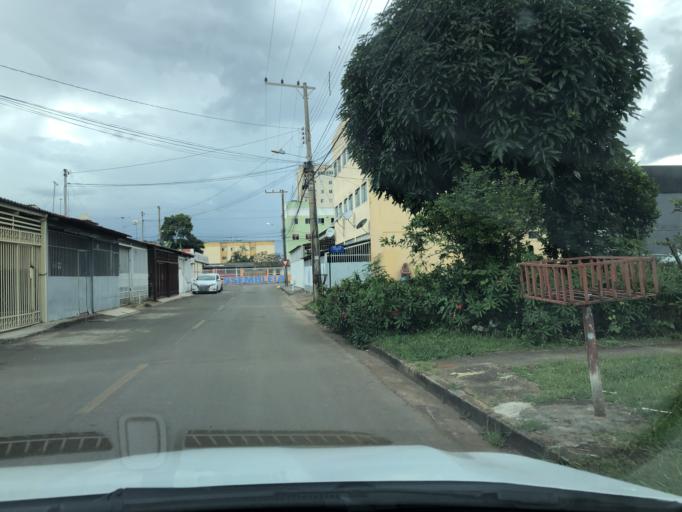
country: BR
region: Federal District
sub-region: Brasilia
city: Brasilia
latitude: -15.8695
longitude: -48.0634
